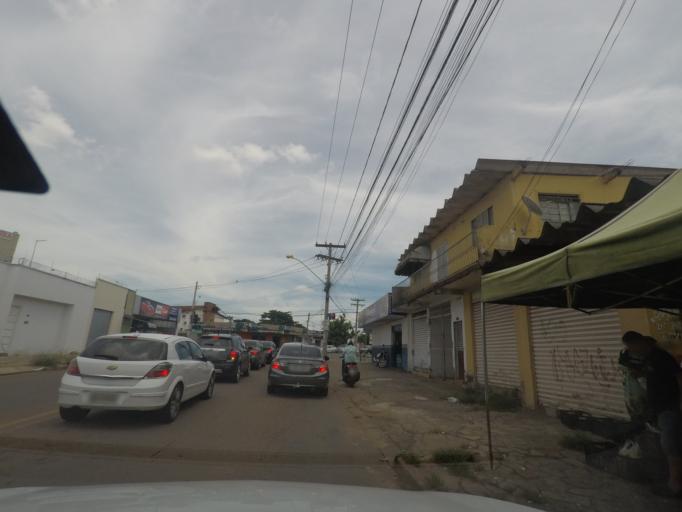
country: BR
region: Goias
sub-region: Goiania
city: Goiania
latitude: -16.6855
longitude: -49.2852
